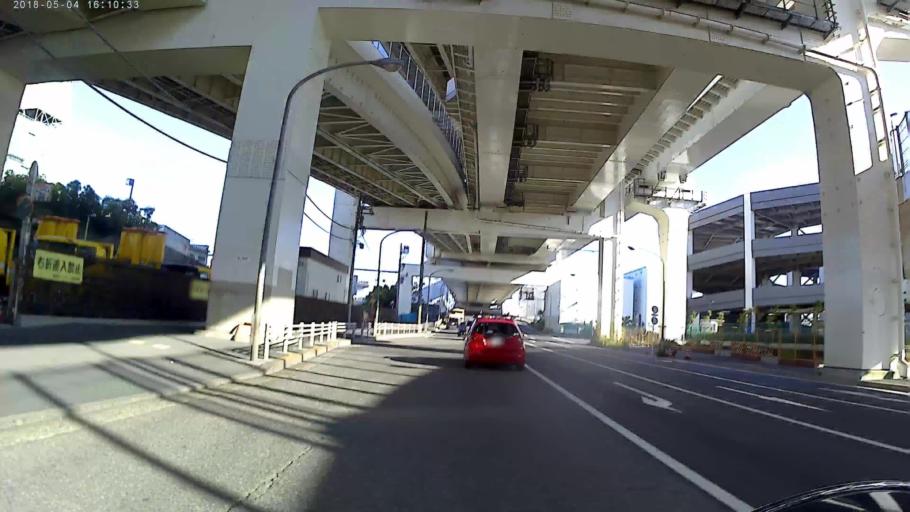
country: JP
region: Kanagawa
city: Yokohama
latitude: 35.4910
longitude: 139.6713
